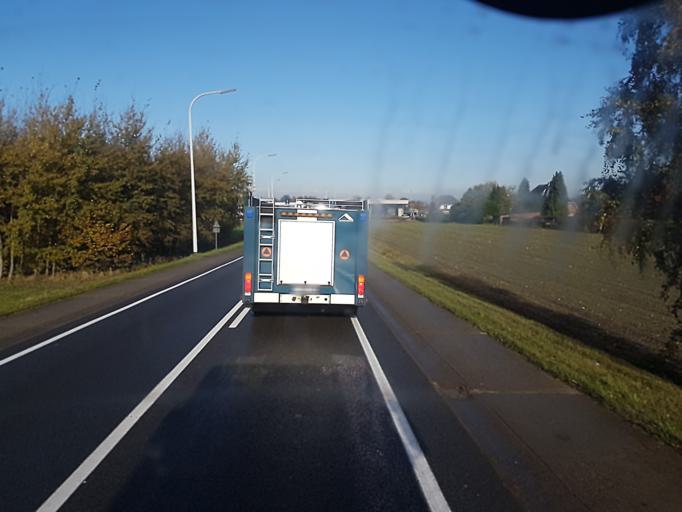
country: BE
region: Flanders
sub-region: Provincie Antwerpen
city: Brecht
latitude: 51.3459
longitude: 4.6714
